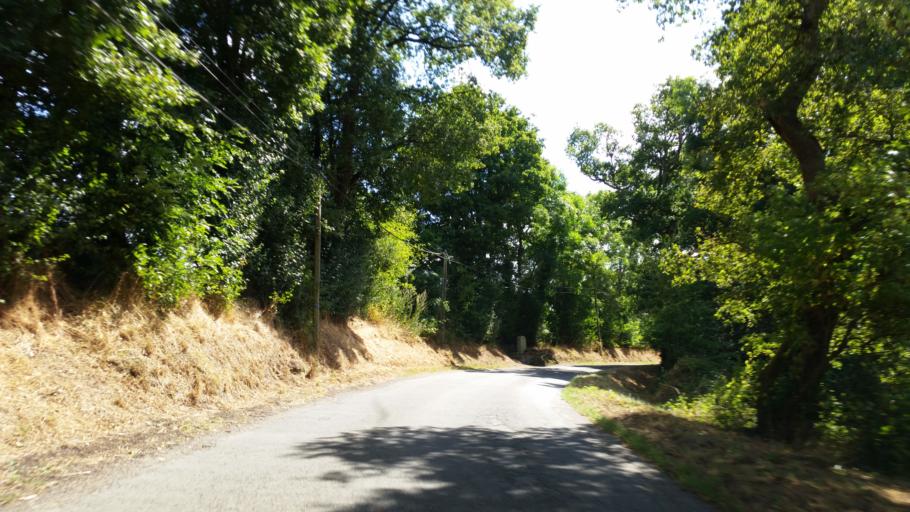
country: FR
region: Lower Normandy
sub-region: Departement du Calvados
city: Clecy
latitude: 48.8454
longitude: -0.3796
